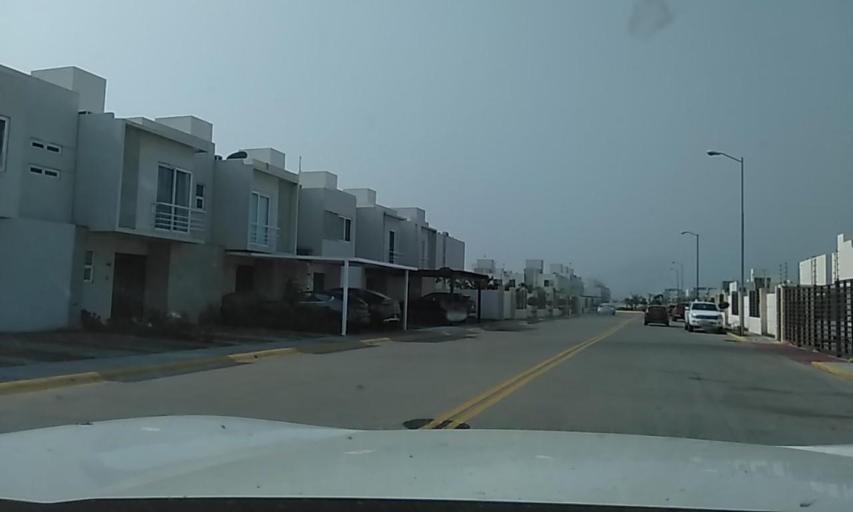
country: MX
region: Veracruz
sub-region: Veracruz
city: Hacienda Sotavento
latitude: 19.1290
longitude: -96.1713
